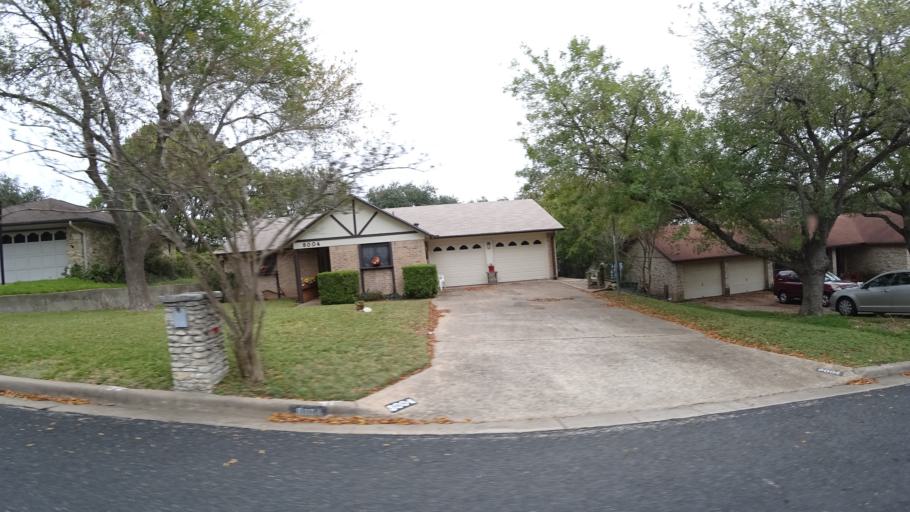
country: US
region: Texas
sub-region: Travis County
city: Barton Creek
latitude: 30.2392
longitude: -97.8902
